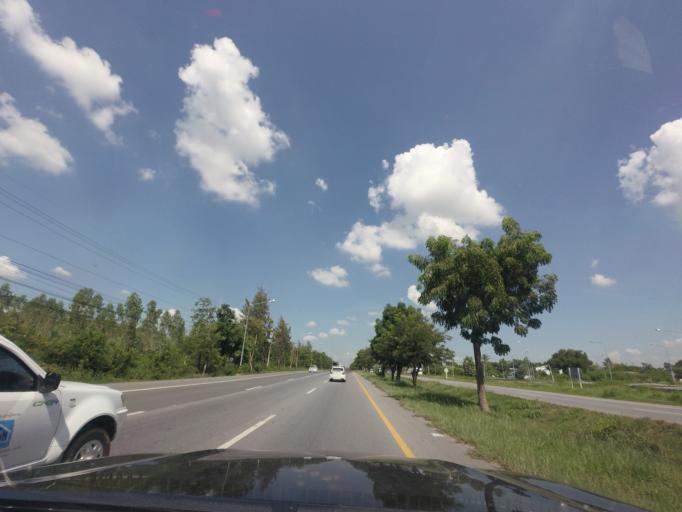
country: TH
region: Nakhon Ratchasima
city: Chaloem Phra Kiat
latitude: 15.0616
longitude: 102.1774
